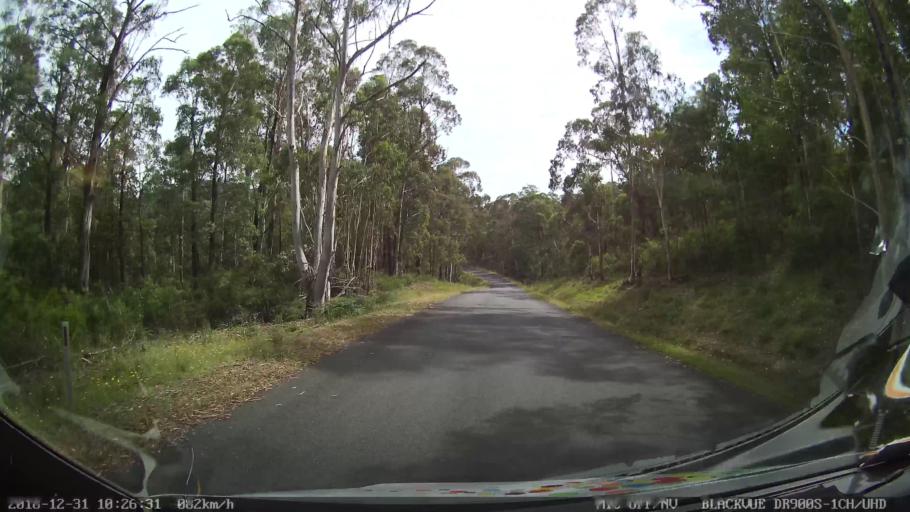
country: AU
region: New South Wales
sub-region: Snowy River
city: Jindabyne
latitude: -36.4946
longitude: 148.1401
